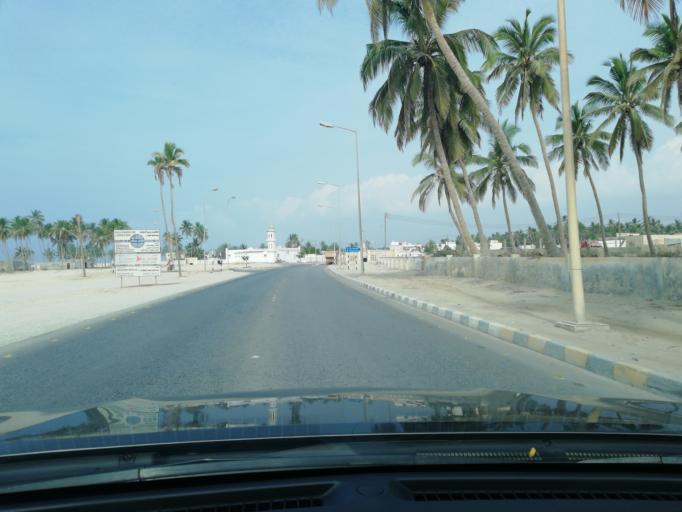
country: OM
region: Zufar
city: Salalah
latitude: 17.0030
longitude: 54.1131
